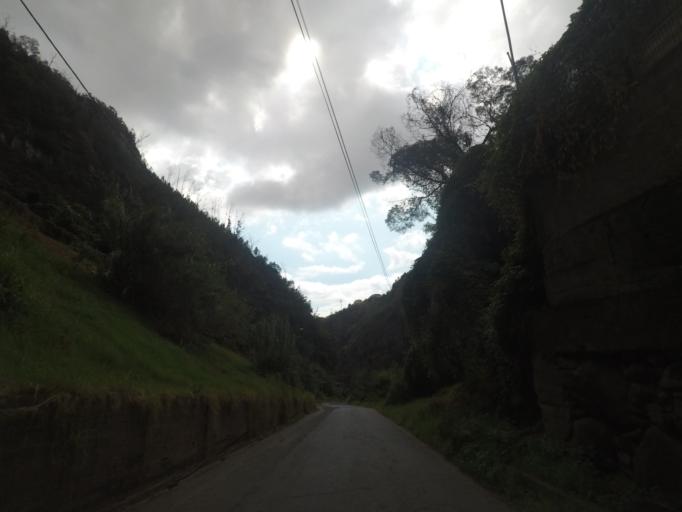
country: PT
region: Madeira
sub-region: Funchal
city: Nossa Senhora do Monte
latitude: 32.6808
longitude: -16.9159
